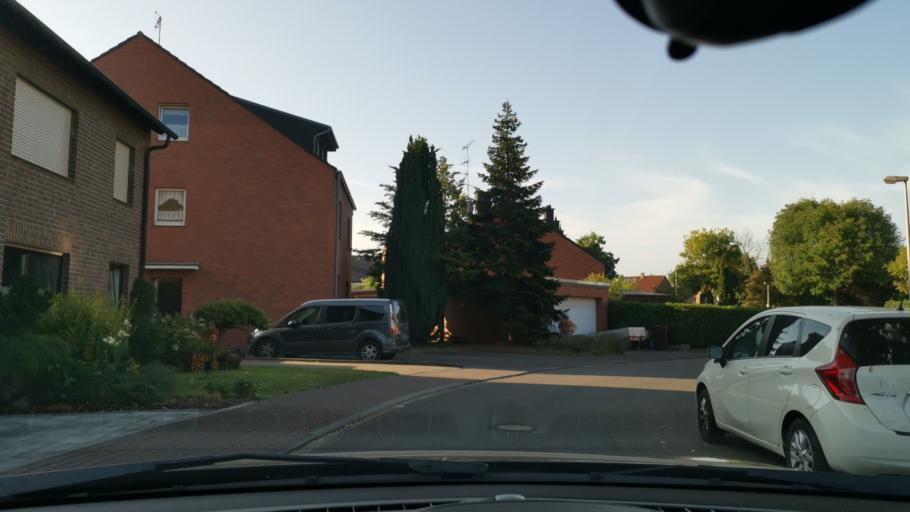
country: DE
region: North Rhine-Westphalia
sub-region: Regierungsbezirk Dusseldorf
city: Dormagen
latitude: 51.1080
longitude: 6.7500
